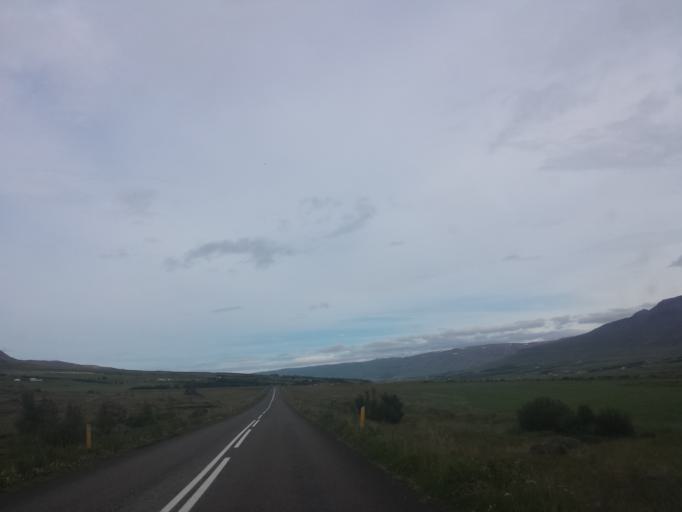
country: IS
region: Northeast
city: Akureyri
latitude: 65.5068
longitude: -18.1703
